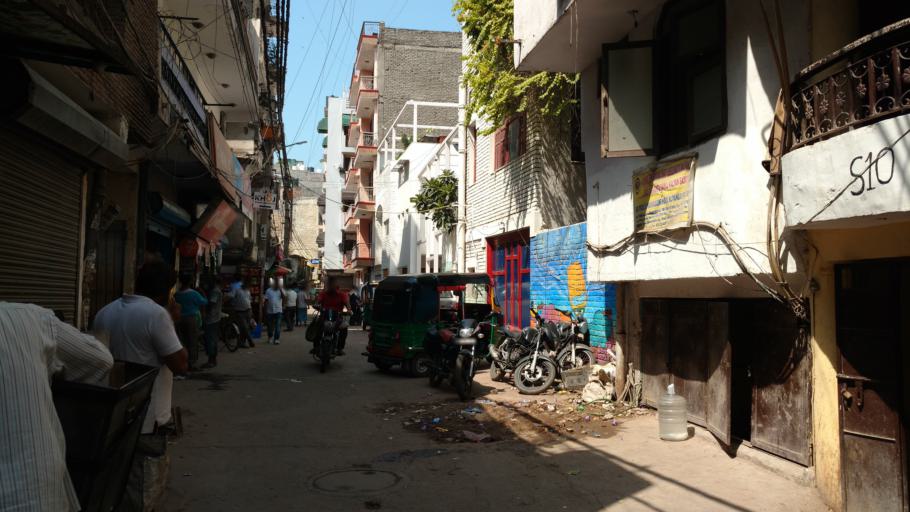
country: IN
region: NCT
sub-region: New Delhi
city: New Delhi
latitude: 28.5310
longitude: 77.2179
